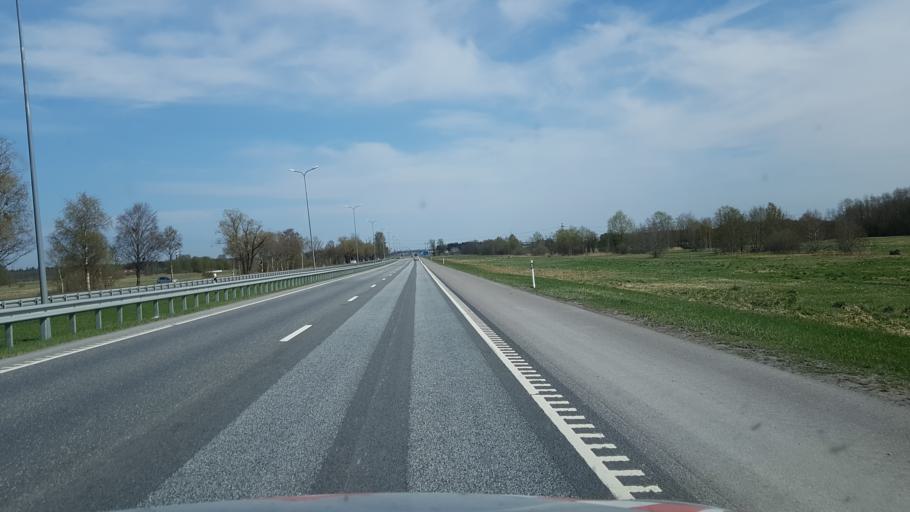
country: EE
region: Harju
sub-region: Saue vald
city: Laagri
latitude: 59.3253
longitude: 24.5930
